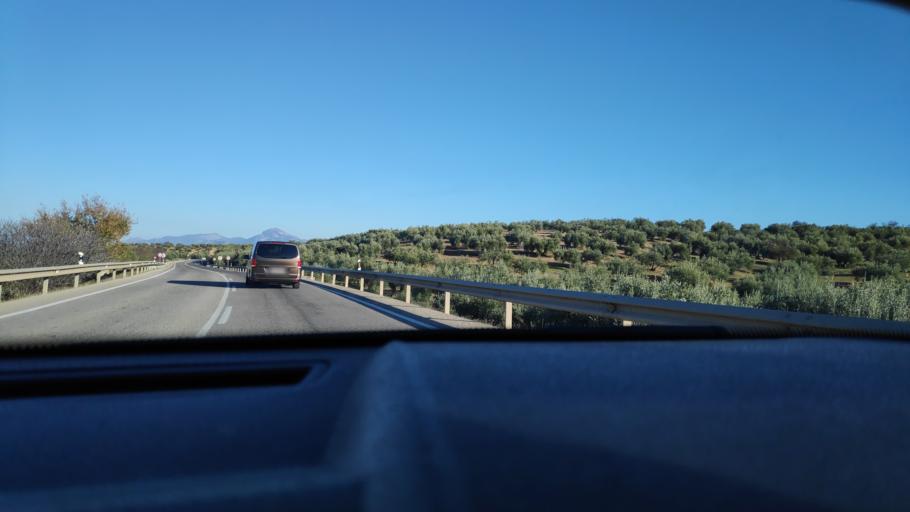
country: ES
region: Andalusia
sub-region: Province of Cordoba
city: Luque
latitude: 37.5673
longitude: -4.2415
